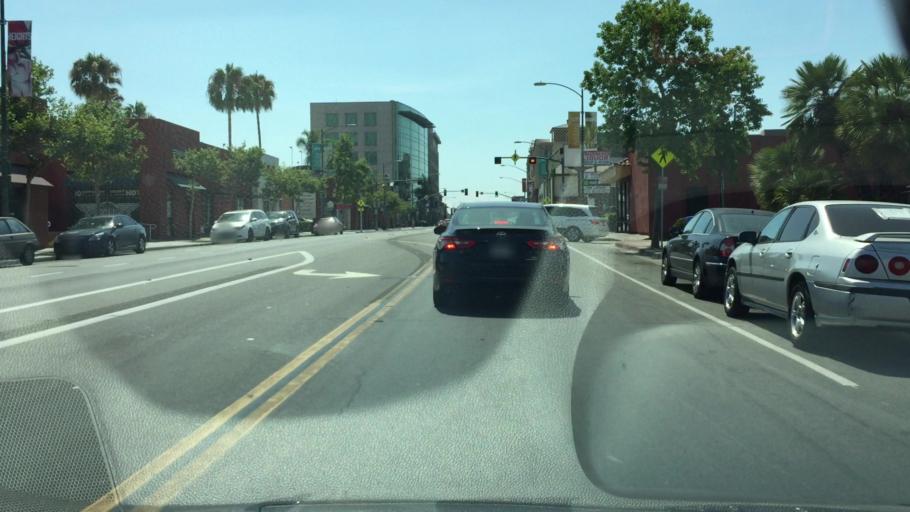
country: US
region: California
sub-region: San Diego County
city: San Diego
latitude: 32.7497
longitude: -117.0989
